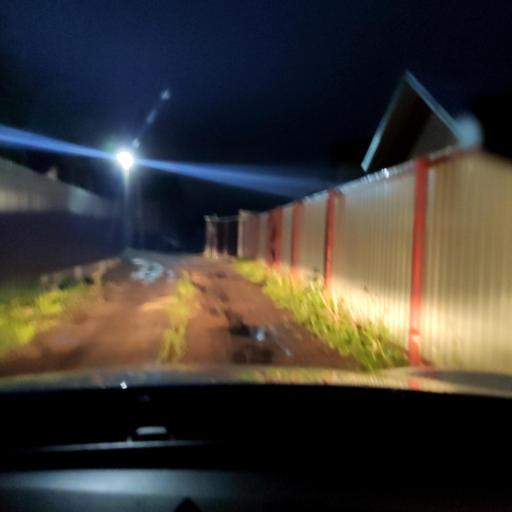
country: RU
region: Tatarstan
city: Stolbishchi
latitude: 55.6485
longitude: 49.2776
